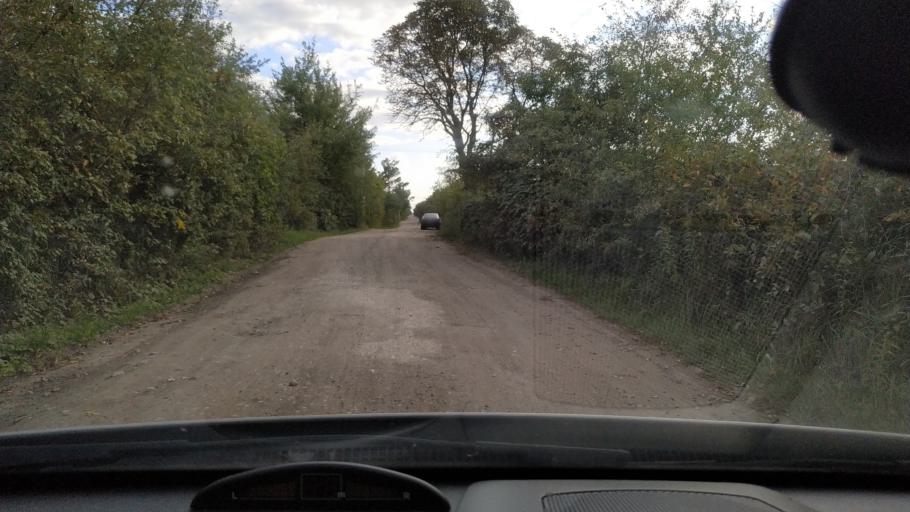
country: RU
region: Rjazan
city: Polyany
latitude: 54.5591
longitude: 39.8778
